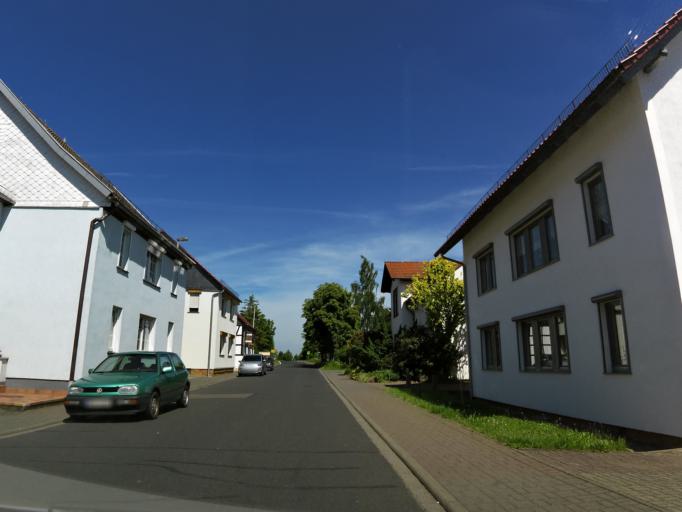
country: DE
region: Thuringia
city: Ernstroda
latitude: 50.8898
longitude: 10.6461
